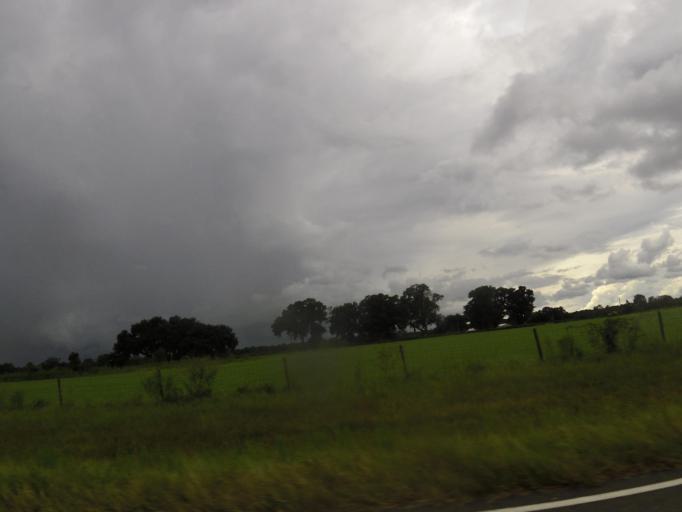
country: US
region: Florida
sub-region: Baker County
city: Macclenny
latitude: 30.4221
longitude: -82.1998
